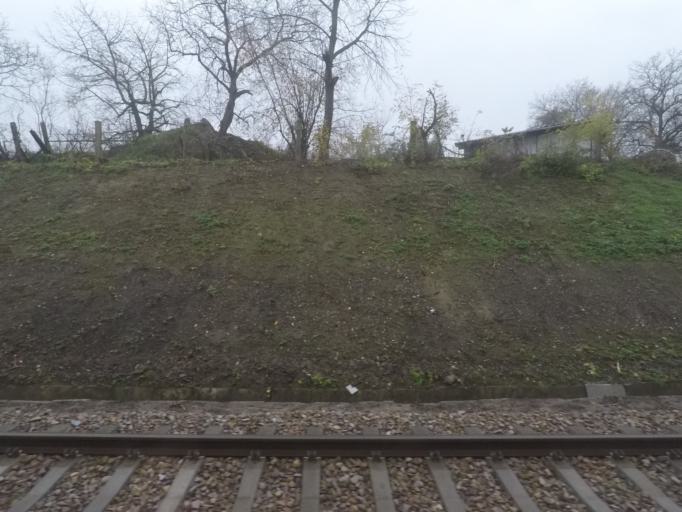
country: PL
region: Lesser Poland Voivodeship
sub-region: Powiat wielicki
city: Kokotow
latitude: 50.0912
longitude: 20.0496
